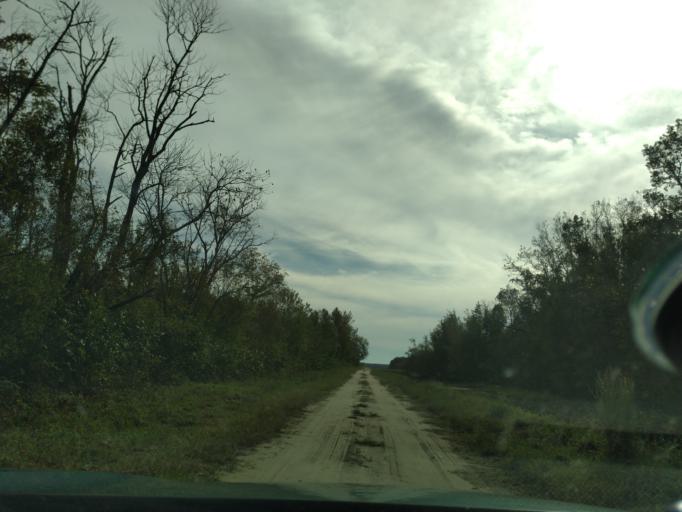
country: US
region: North Carolina
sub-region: Beaufort County
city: Belhaven
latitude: 35.7203
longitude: -76.5751
